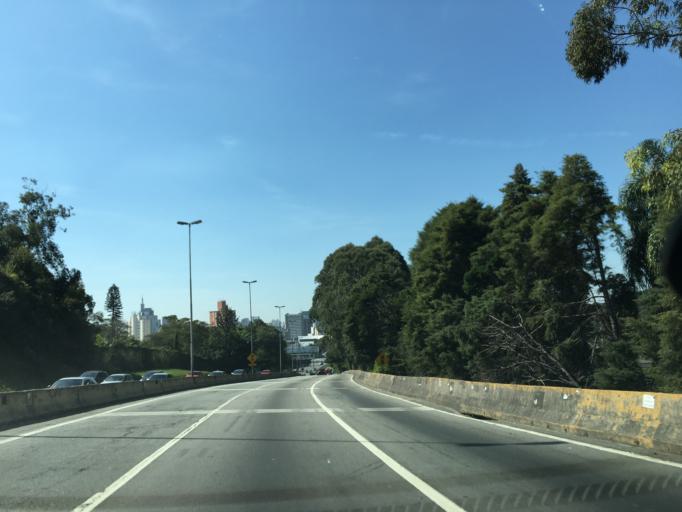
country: BR
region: Sao Paulo
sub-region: Sao Paulo
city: Sao Paulo
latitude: -23.5744
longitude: -46.7157
